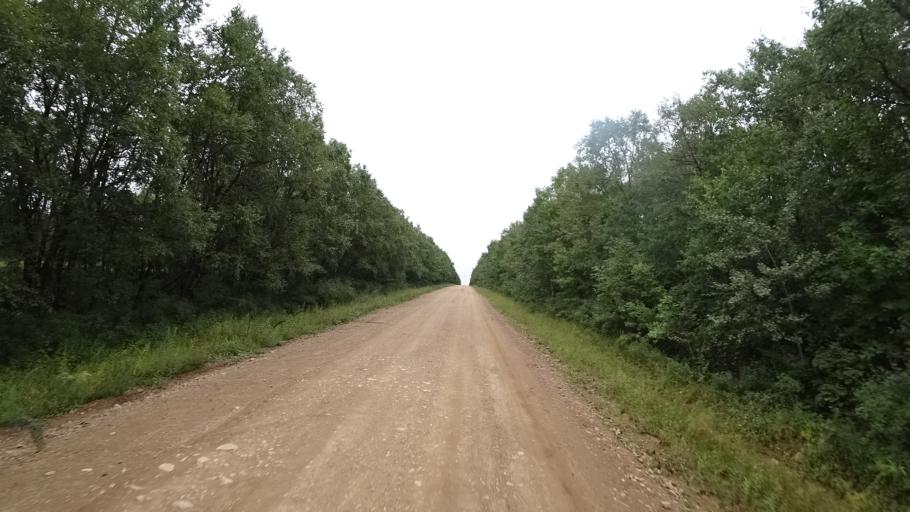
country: RU
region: Primorskiy
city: Ivanovka
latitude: 44.0289
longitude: 132.5280
